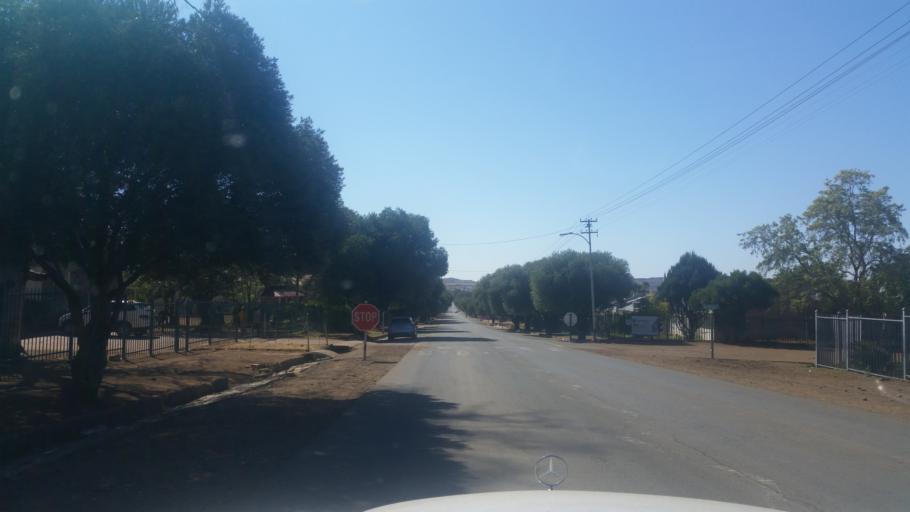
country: ZA
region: Orange Free State
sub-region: Xhariep District Municipality
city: Trompsburg
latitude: -30.4949
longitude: 25.9690
